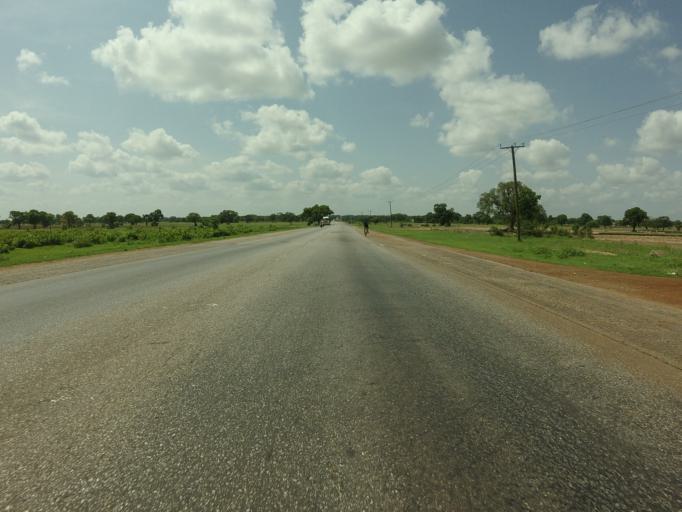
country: GH
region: Northern
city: Savelugu
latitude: 9.5563
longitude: -0.8369
